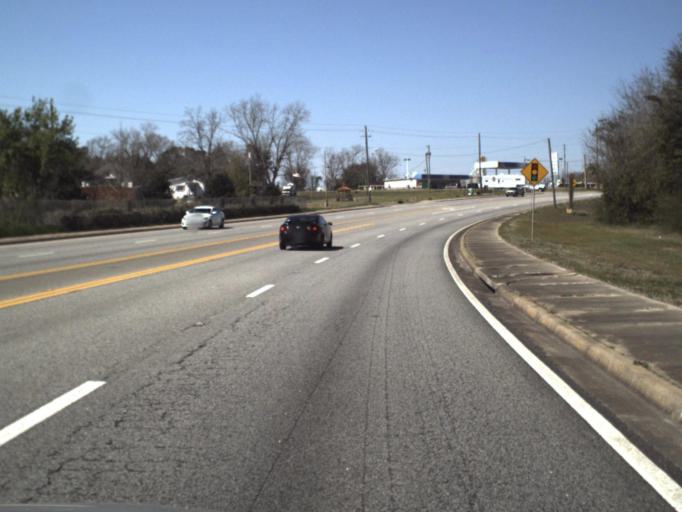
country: US
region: Florida
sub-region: Jackson County
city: Graceville
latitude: 30.9473
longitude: -85.4011
